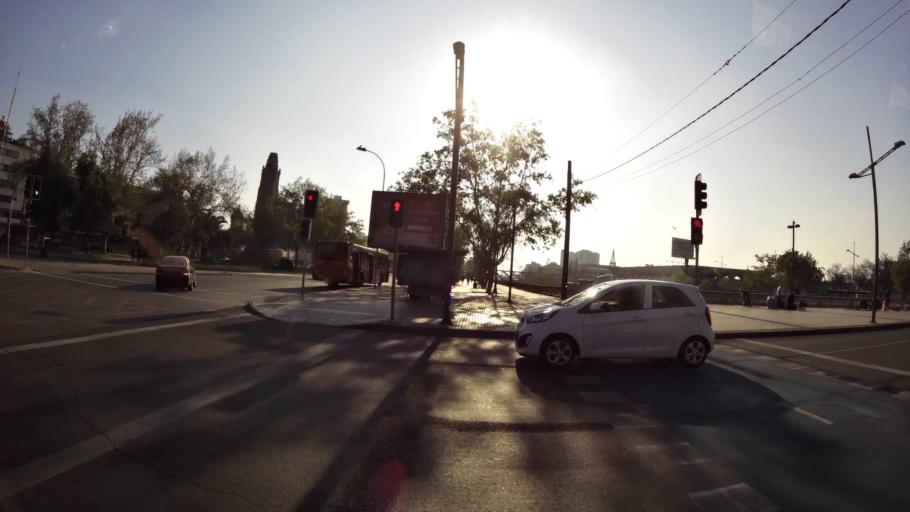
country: CL
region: Santiago Metropolitan
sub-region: Provincia de Santiago
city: Santiago
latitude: -33.4332
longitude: -70.6487
